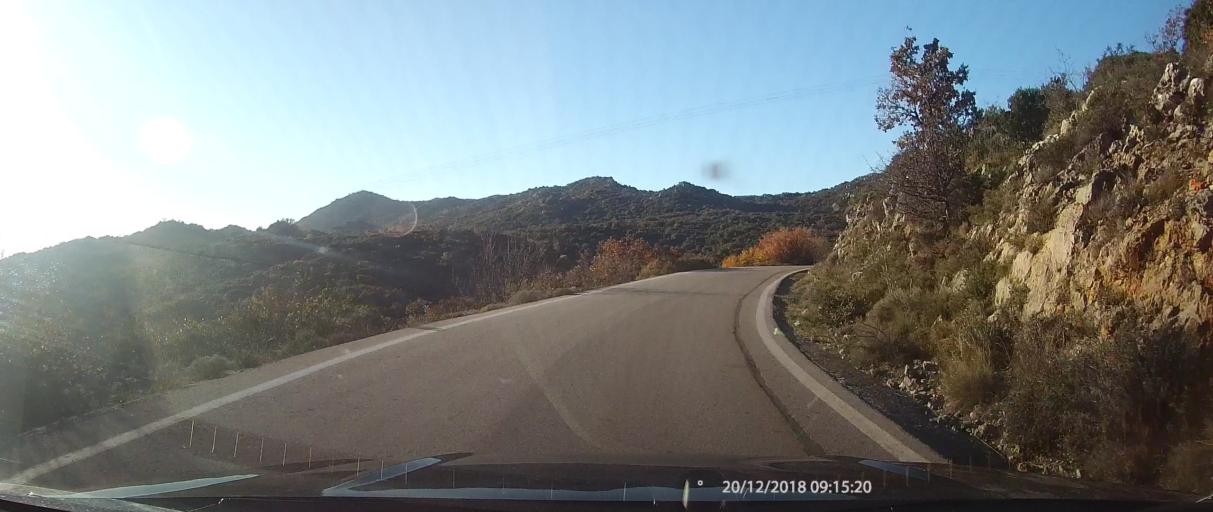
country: GR
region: Peloponnese
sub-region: Nomos Lakonias
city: Sykea
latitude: 36.9023
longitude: 22.9791
